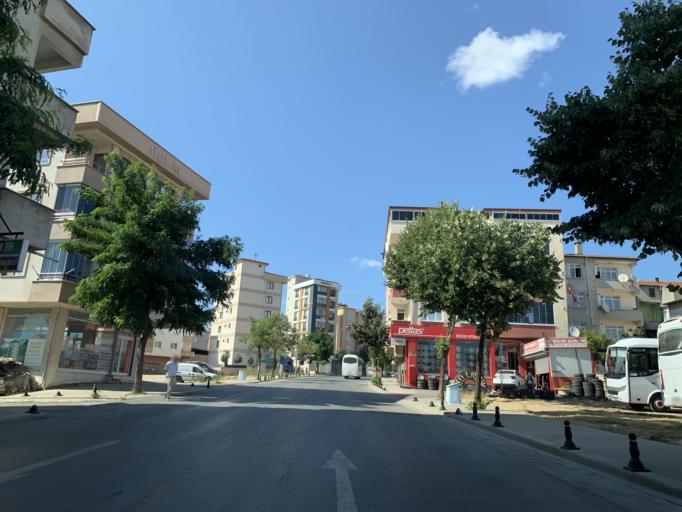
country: TR
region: Istanbul
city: Pendik
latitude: 40.8820
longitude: 29.2823
